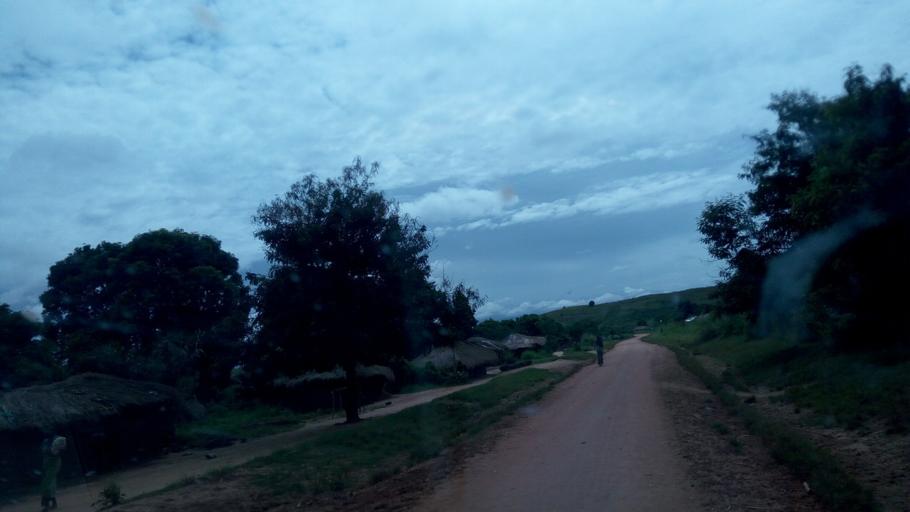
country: CD
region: Katanga
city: Kalemie
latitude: -5.9758
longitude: 29.1201
